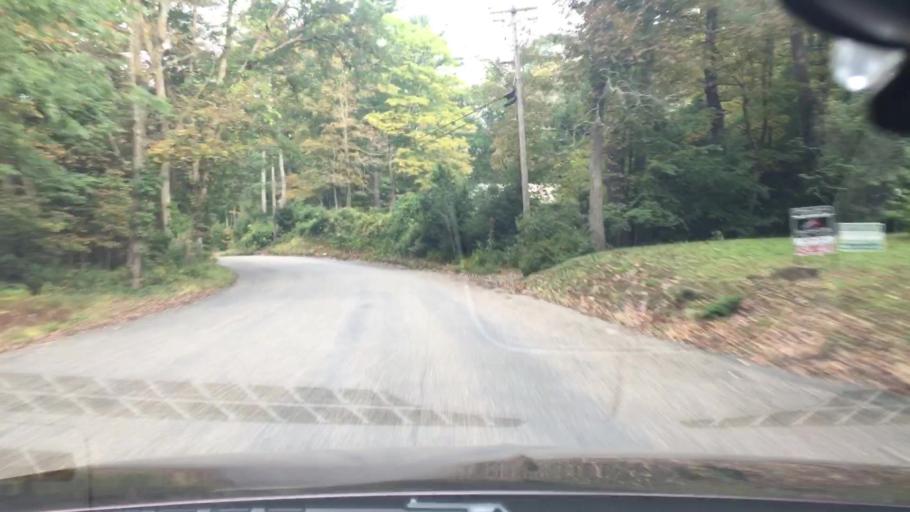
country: US
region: Connecticut
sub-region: Tolland County
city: Stafford
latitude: 41.9940
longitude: -72.3135
